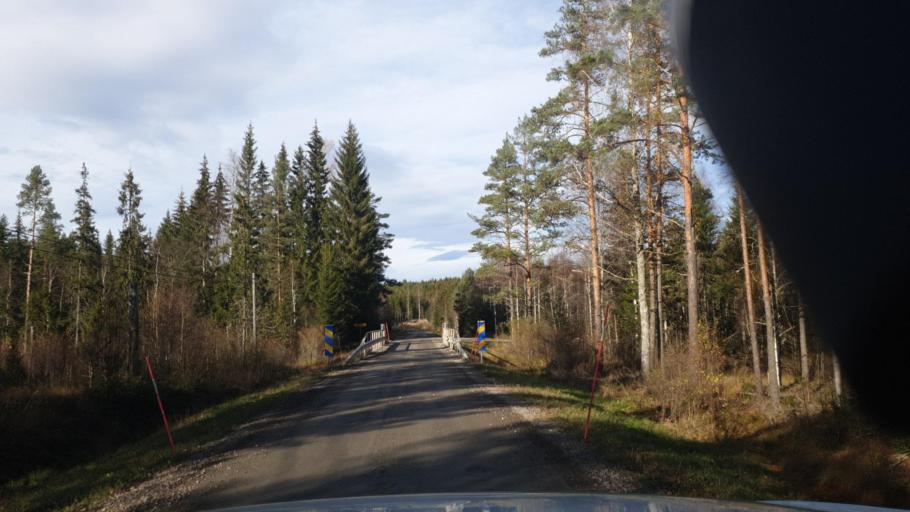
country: SE
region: Vaermland
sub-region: Eda Kommun
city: Charlottenberg
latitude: 59.9681
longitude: 12.5038
